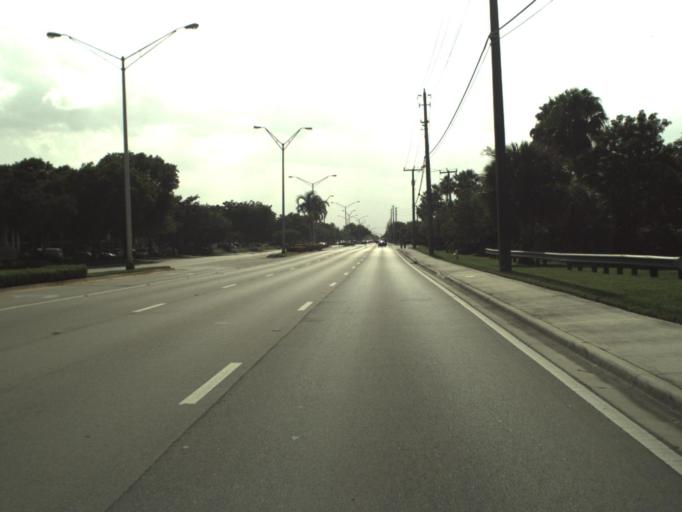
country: US
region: Florida
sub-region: Broward County
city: Coral Springs
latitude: 26.2728
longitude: -80.2737
